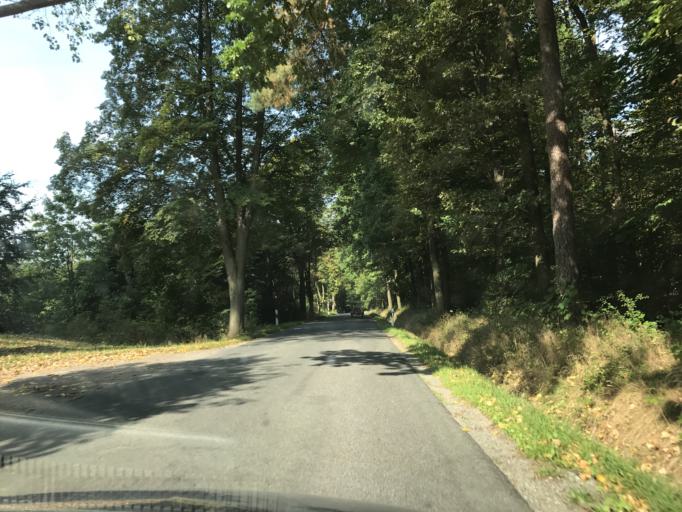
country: DE
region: Saxony
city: Lobau
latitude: 51.0878
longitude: 14.6810
